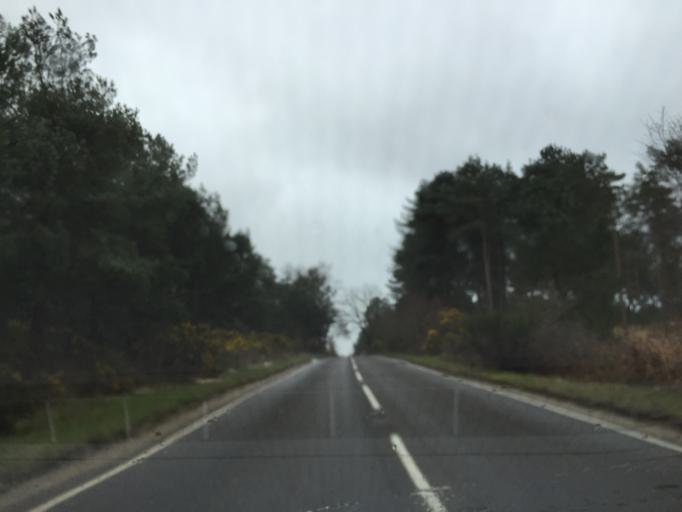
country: GB
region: England
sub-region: Dorset
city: St Leonards
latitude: 50.8636
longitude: -1.8353
